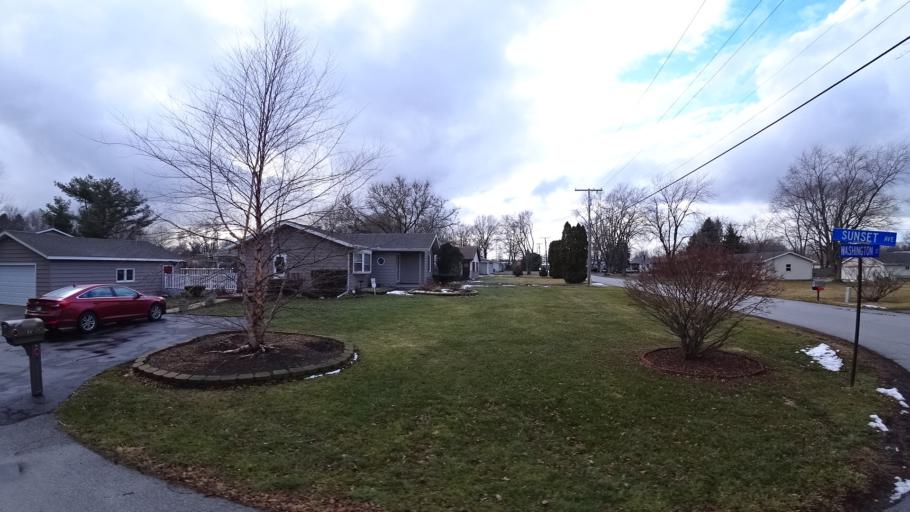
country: US
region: Indiana
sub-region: Porter County
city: Porter
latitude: 41.6123
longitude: -87.0931
